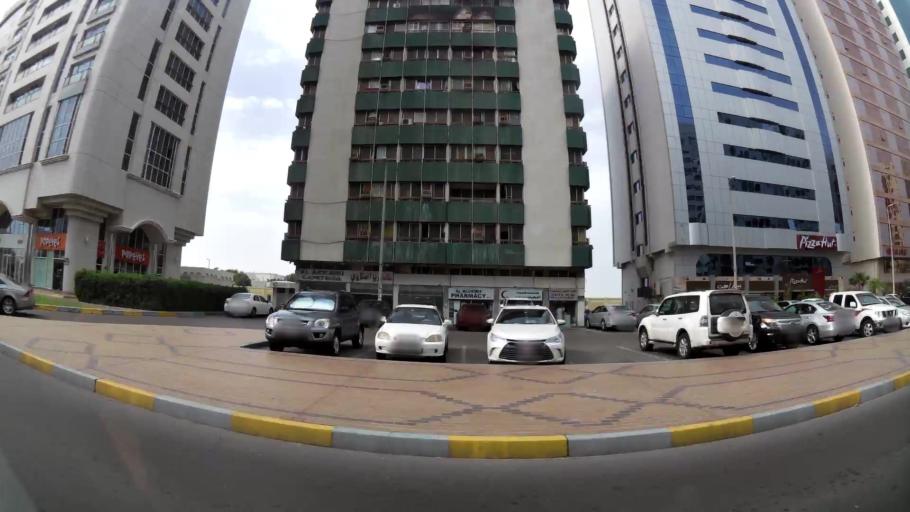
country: AE
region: Abu Dhabi
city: Abu Dhabi
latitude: 24.4591
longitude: 54.3810
